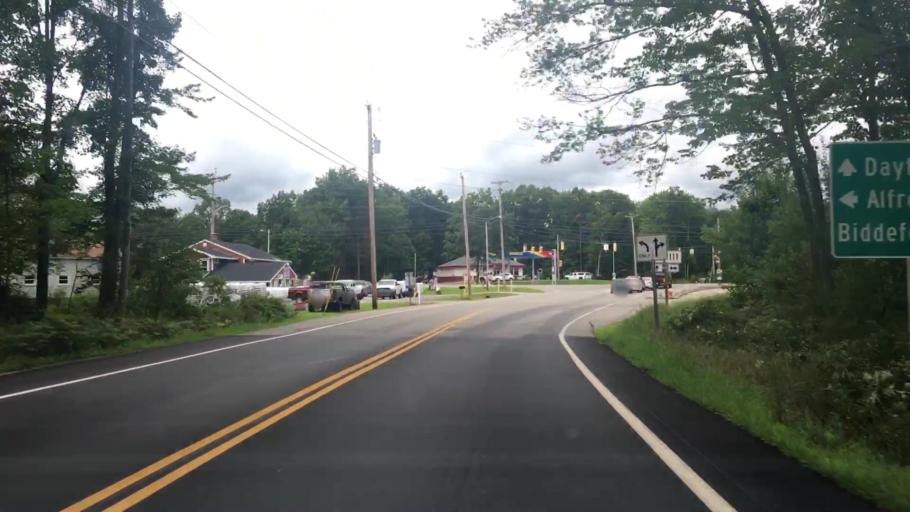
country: US
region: Maine
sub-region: York County
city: West Kennebunk
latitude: 43.4783
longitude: -70.6044
